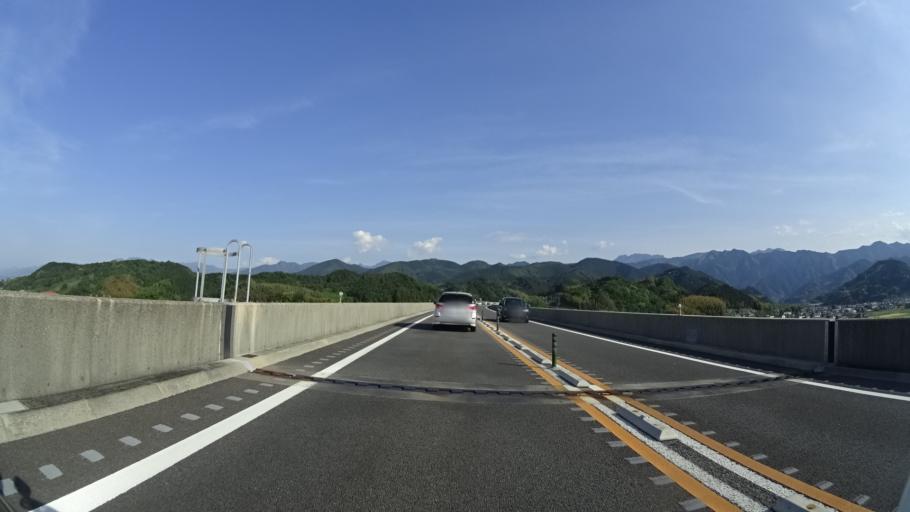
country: JP
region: Ehime
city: Saijo
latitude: 33.8916
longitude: 133.0847
